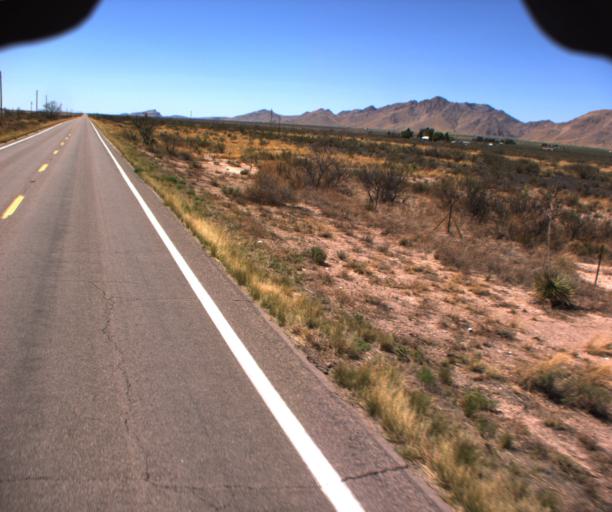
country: US
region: New Mexico
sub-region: Hidalgo County
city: Lordsburg
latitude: 31.7956
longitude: -109.0598
